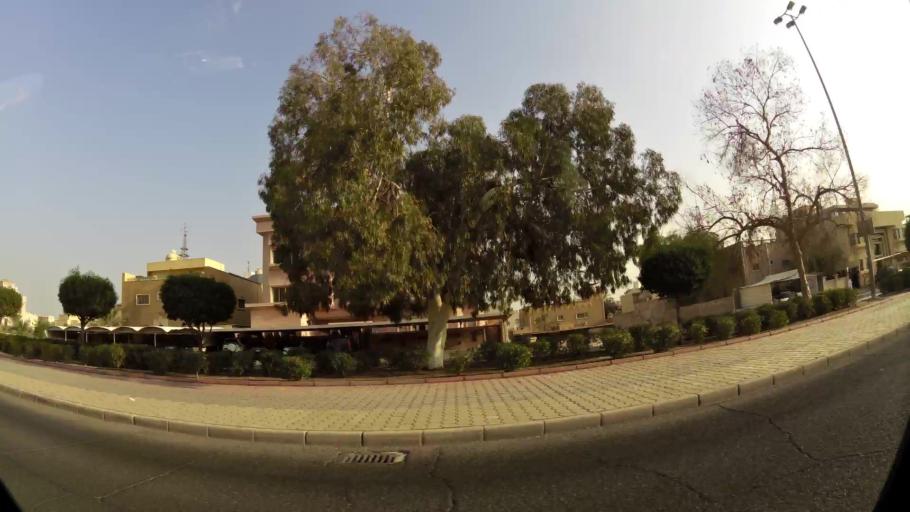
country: KW
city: Bayan
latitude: 29.3109
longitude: 48.0590
